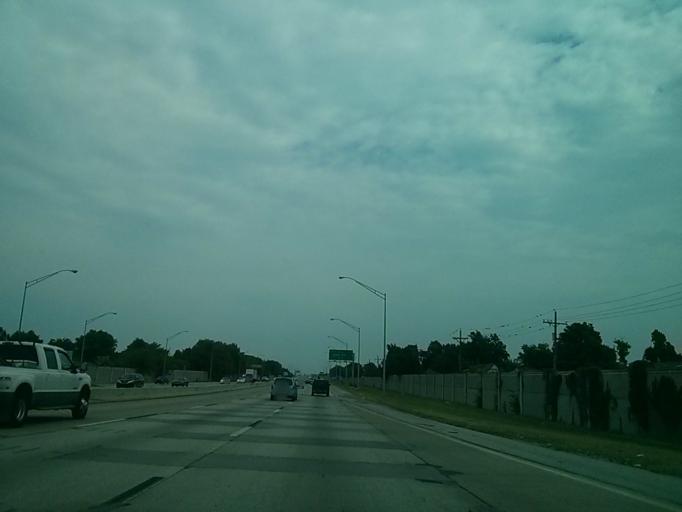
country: US
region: Oklahoma
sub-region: Tulsa County
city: Broken Arrow
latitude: 36.1208
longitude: -95.8597
